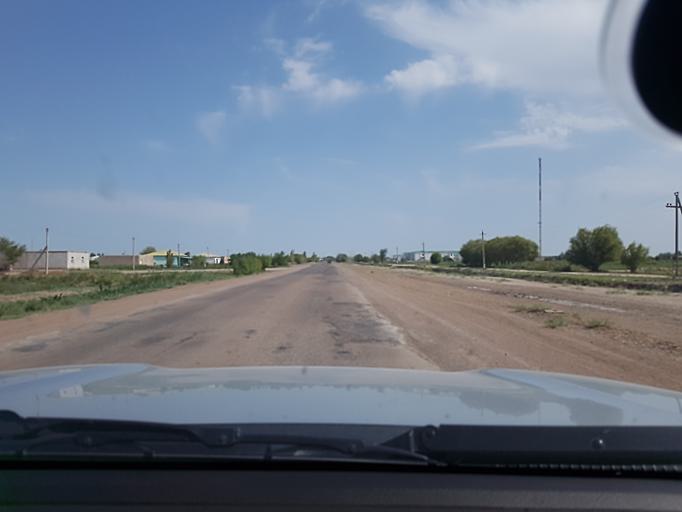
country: TM
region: Dasoguz
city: Boldumsaz
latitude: 42.1414
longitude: 59.6468
